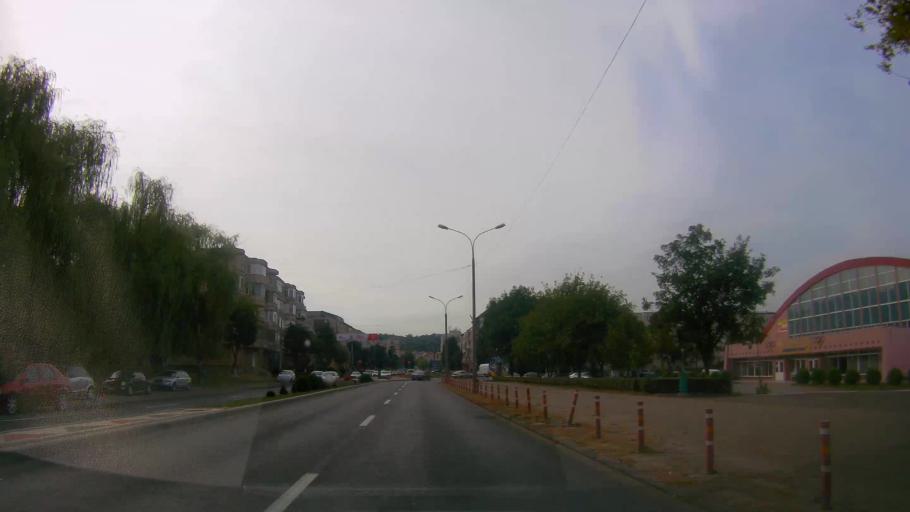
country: RO
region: Salaj
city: Zalau
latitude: 47.1963
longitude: 23.0602
